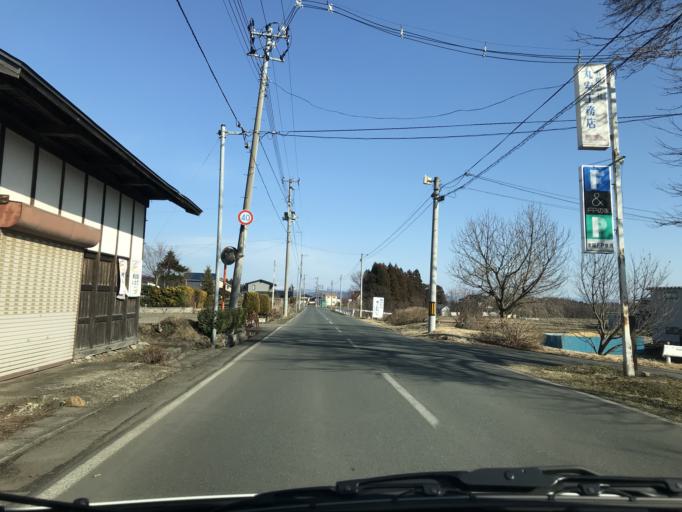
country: JP
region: Iwate
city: Kitakami
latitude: 39.2957
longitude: 141.0404
